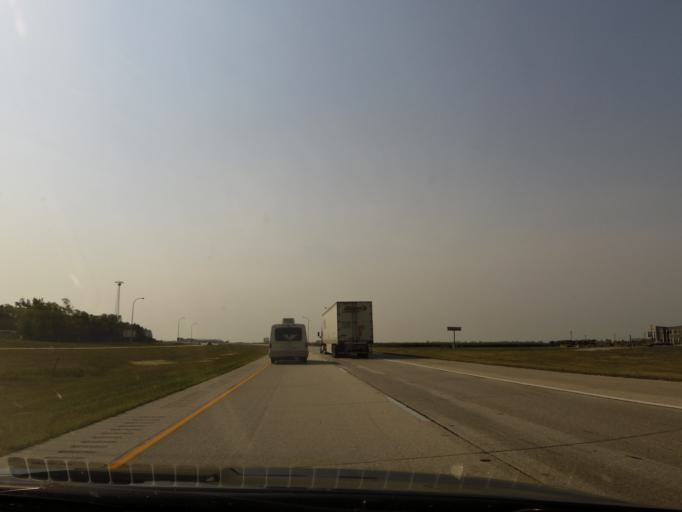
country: US
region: North Dakota
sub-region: Traill County
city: Hillsboro
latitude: 47.4028
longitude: -97.0746
